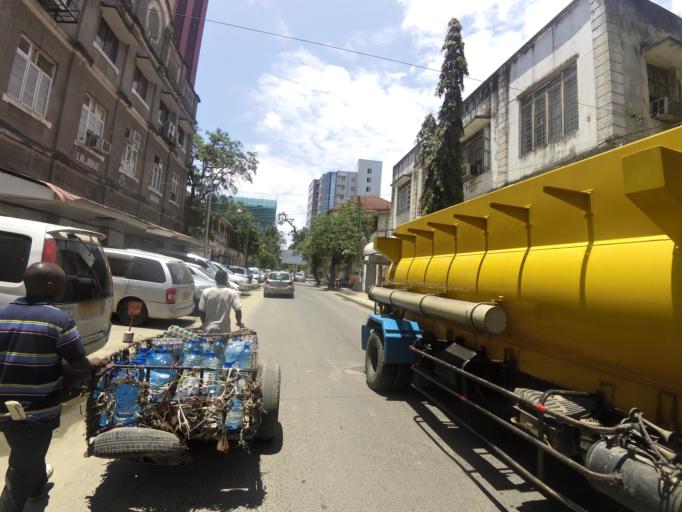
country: TZ
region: Dar es Salaam
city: Dar es Salaam
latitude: -6.8164
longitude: 39.2872
